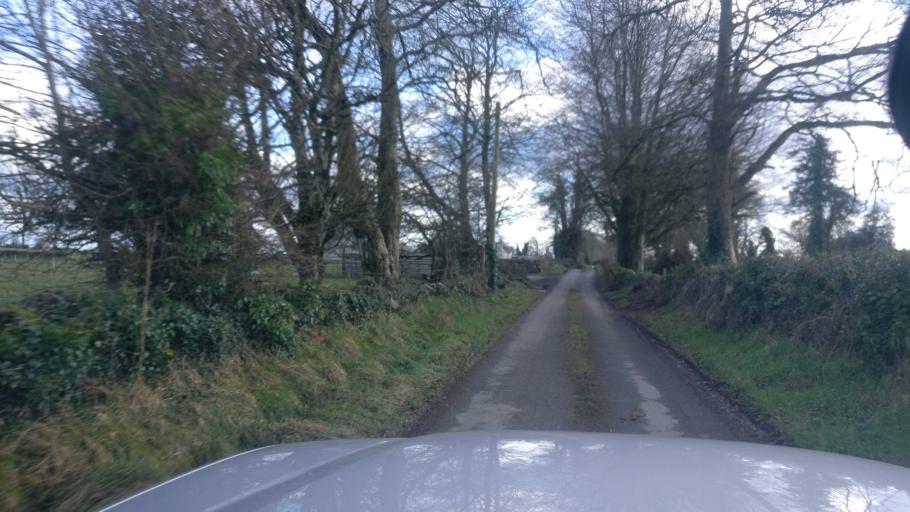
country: IE
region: Connaught
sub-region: County Galway
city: Loughrea
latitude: 53.1806
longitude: -8.4257
